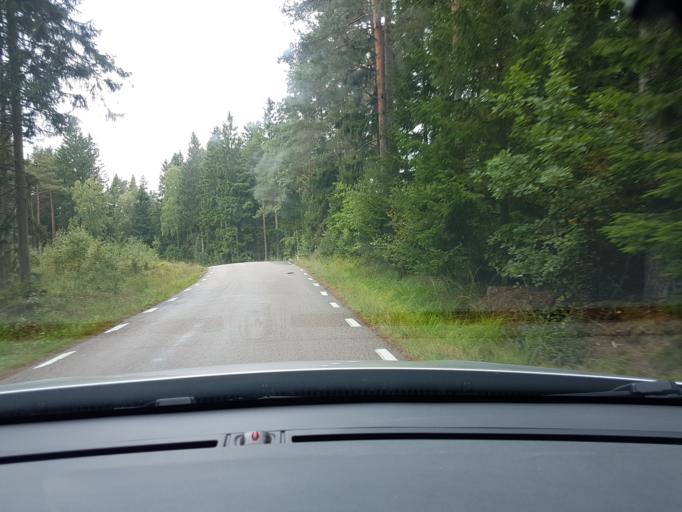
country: SE
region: Vaestra Goetaland
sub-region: Ale Kommun
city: Alvangen
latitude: 57.9077
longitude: 12.1684
